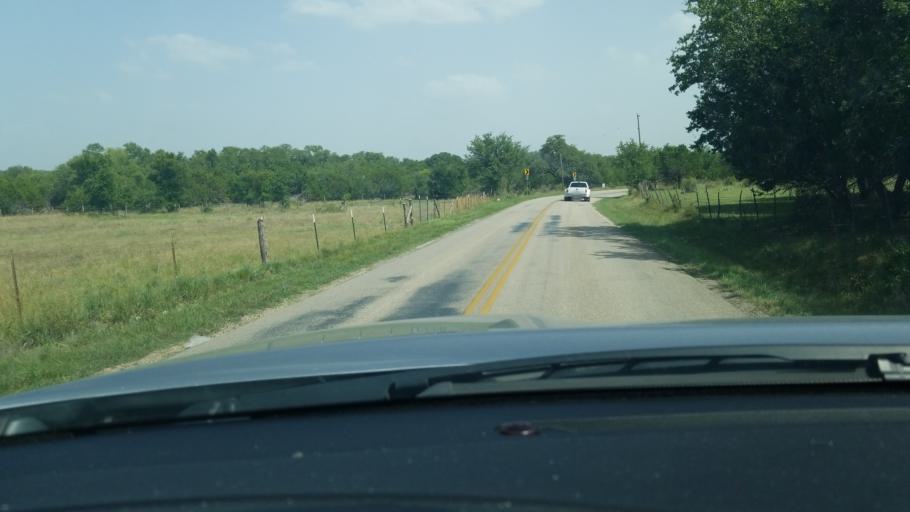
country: US
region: Texas
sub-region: Comal County
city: Bulverde
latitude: 29.7510
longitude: -98.4582
